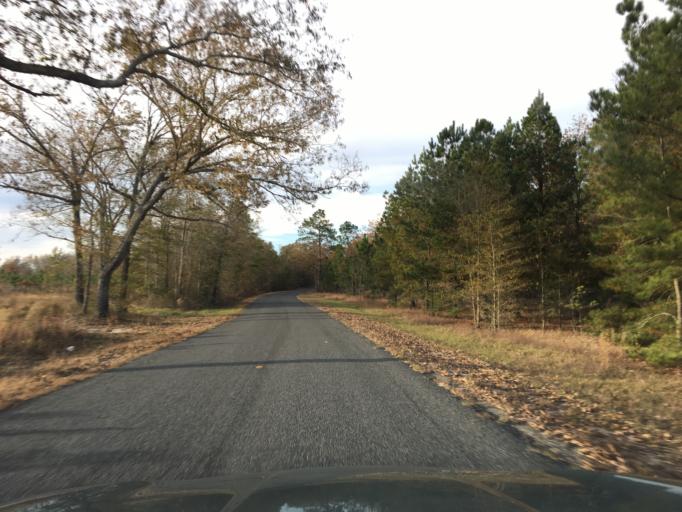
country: US
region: South Carolina
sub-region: Lexington County
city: Leesville
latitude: 33.6803
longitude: -81.3762
